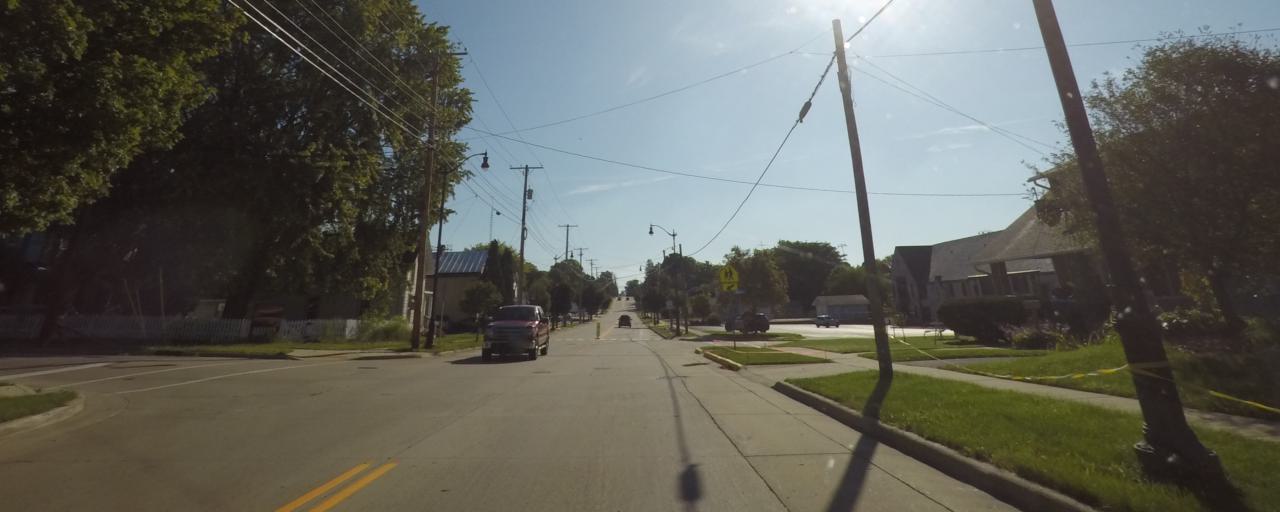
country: US
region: Wisconsin
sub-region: Jefferson County
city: Jefferson
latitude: 43.0052
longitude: -88.8039
